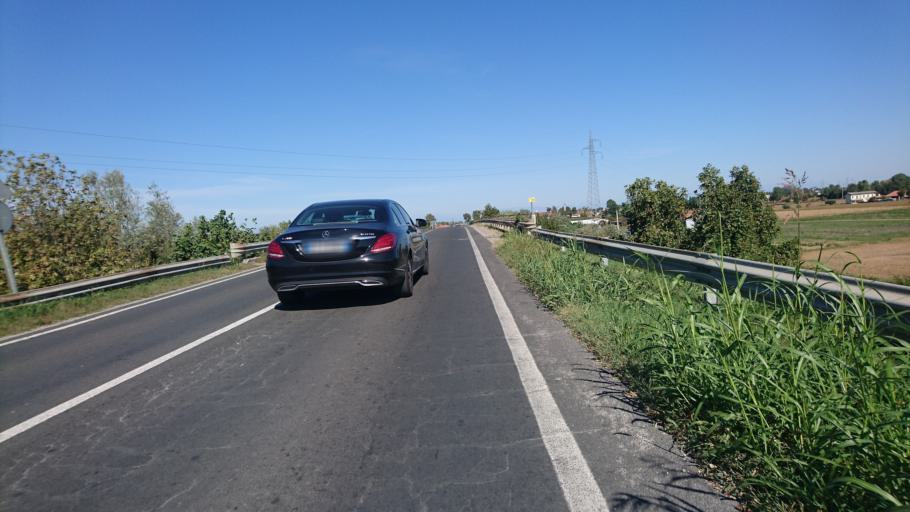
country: IT
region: Veneto
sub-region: Provincia di Venezia
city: Fosso
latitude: 45.4018
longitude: 12.0521
